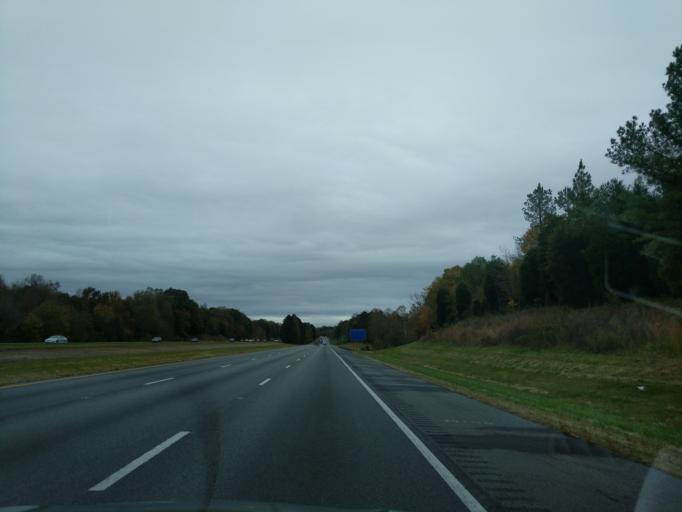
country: US
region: North Carolina
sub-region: Davidson County
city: Lexington
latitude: 35.7994
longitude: -80.2051
